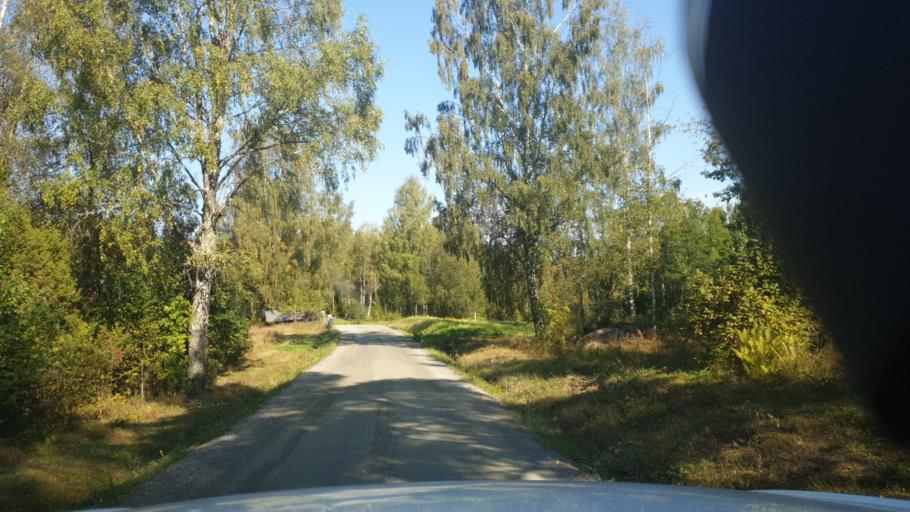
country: SE
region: Vaermland
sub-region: Karlstads Kommun
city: Edsvalla
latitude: 59.6243
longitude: 13.0630
